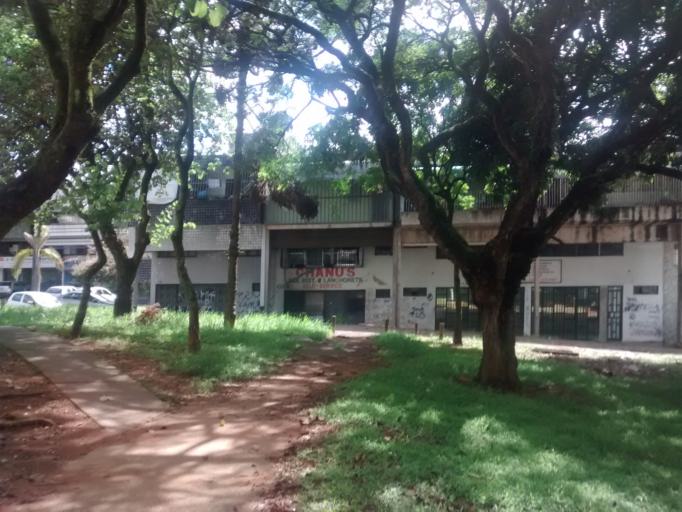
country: BR
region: Federal District
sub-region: Brasilia
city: Brasilia
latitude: -15.7524
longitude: -47.8958
